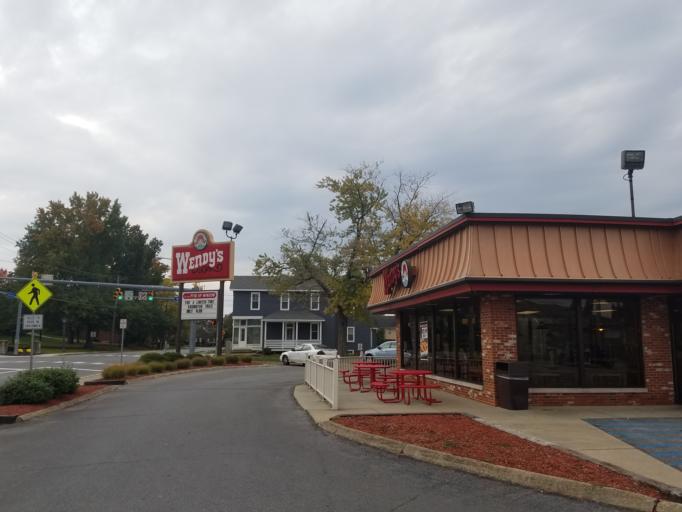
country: US
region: Pennsylvania
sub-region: Clarion County
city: Clarion
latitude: 41.2119
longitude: -79.3810
